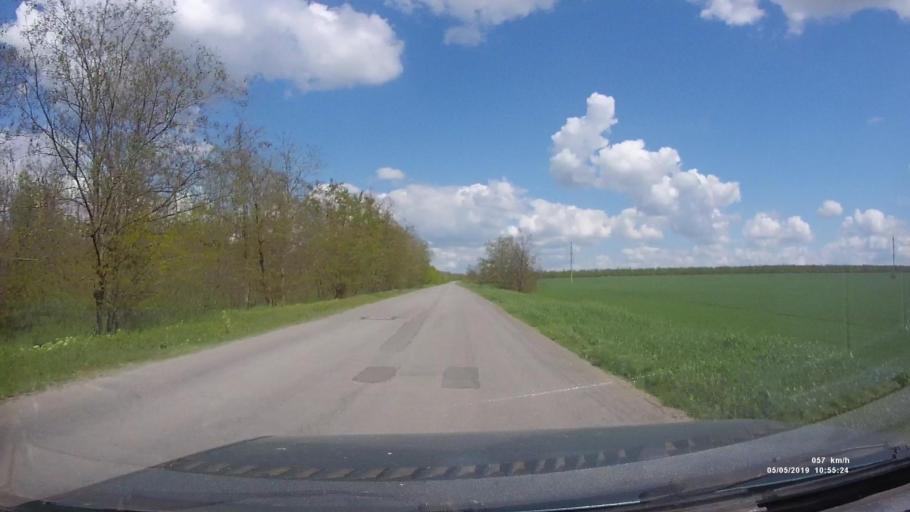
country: RU
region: Rostov
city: Ust'-Donetskiy
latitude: 47.6652
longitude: 40.8212
